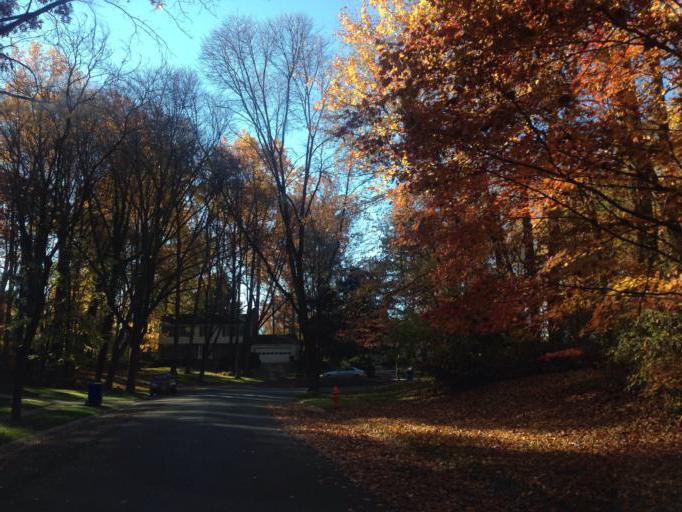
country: US
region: Maryland
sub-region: Howard County
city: Riverside
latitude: 39.1915
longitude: -76.8788
